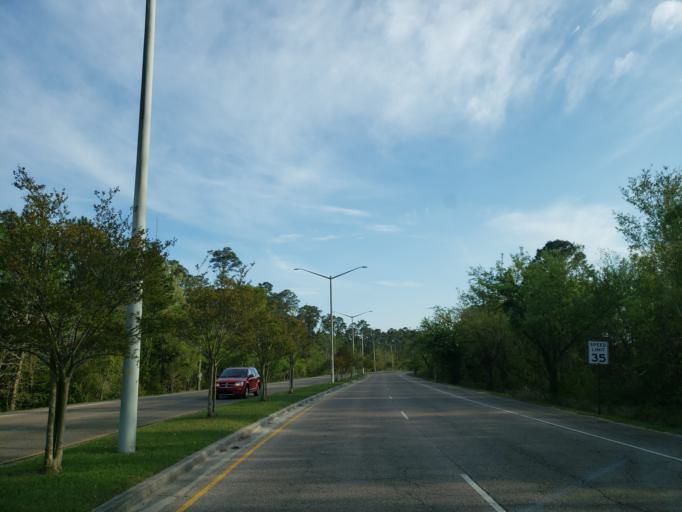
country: US
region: Mississippi
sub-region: Harrison County
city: West Gulfport
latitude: 30.4136
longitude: -89.0577
